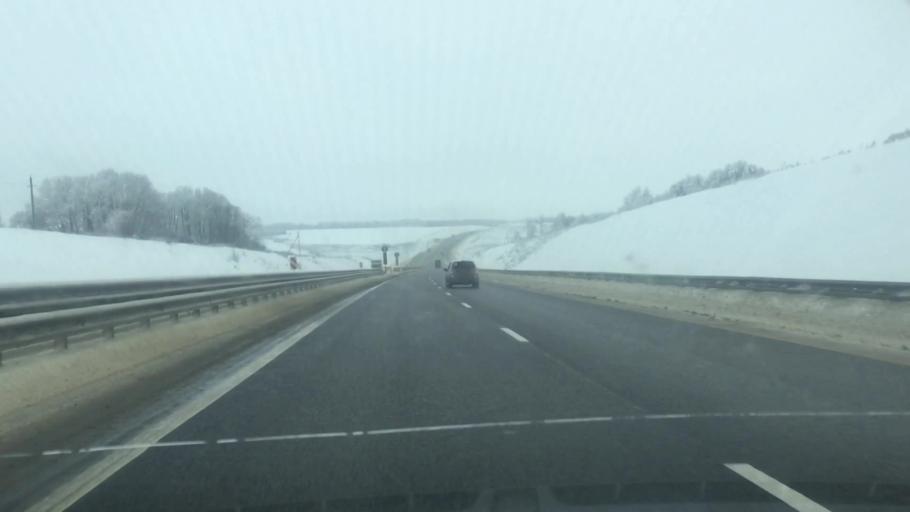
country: RU
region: Lipetsk
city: Stanovoye
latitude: 52.8714
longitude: 38.2801
